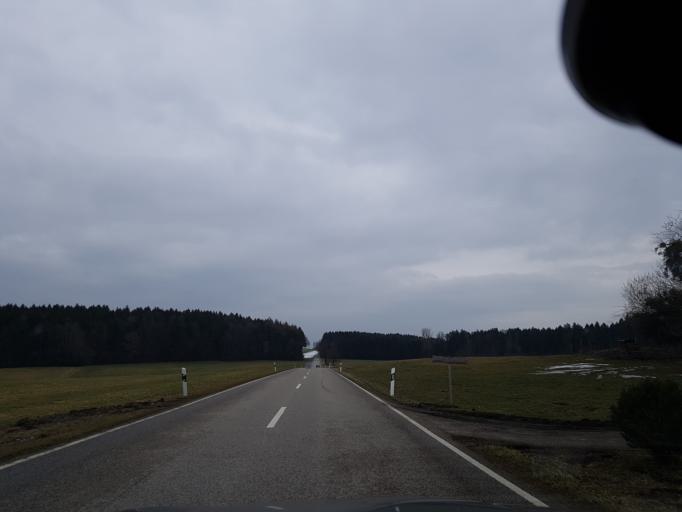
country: DE
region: Bavaria
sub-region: Upper Bavaria
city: Feldkirchen-Westerham
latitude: 47.9406
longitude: 11.8215
